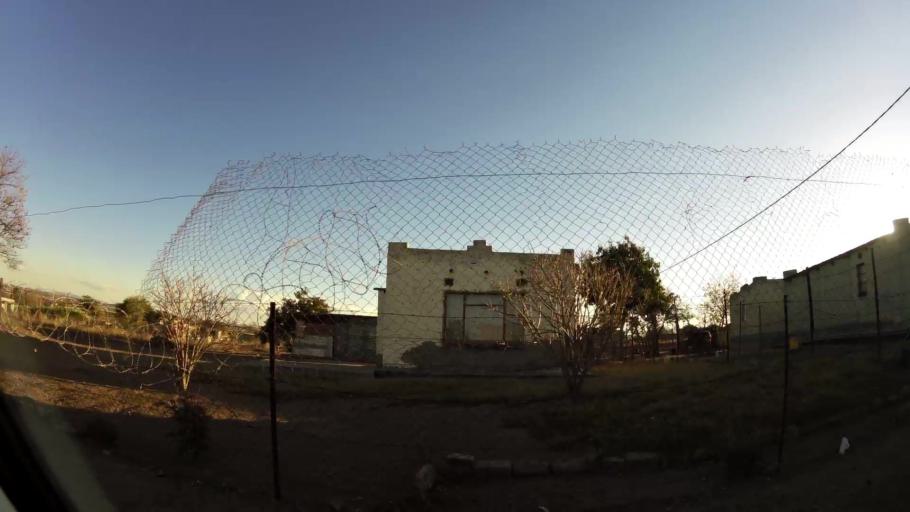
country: ZA
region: Limpopo
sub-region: Capricorn District Municipality
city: Polokwane
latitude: -23.8234
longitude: 29.3784
